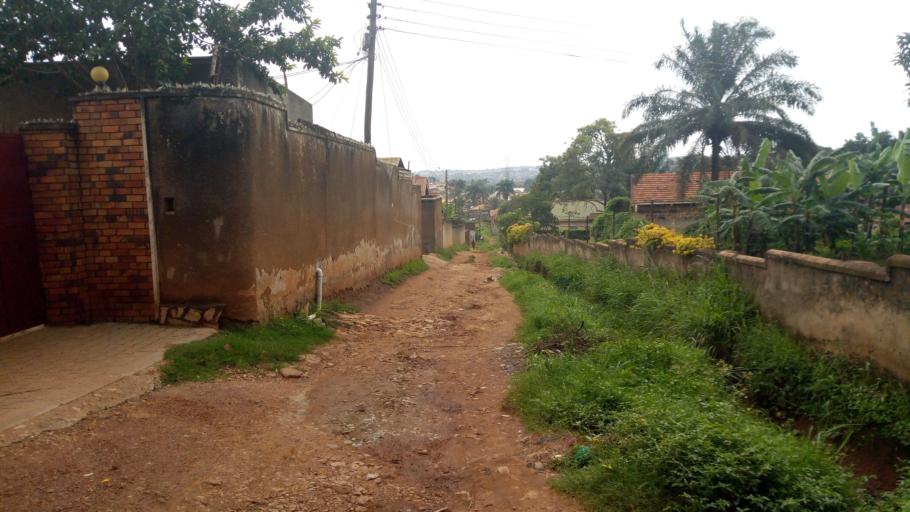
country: UG
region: Central Region
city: Kampala Central Division
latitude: 0.3452
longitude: 32.5602
